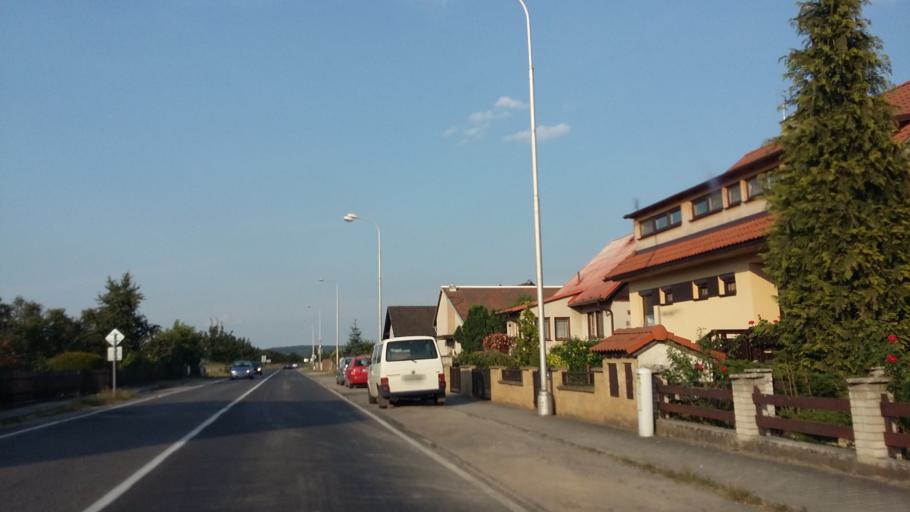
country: CZ
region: Central Bohemia
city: Bakov nad Jizerou
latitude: 50.4738
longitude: 14.9453
